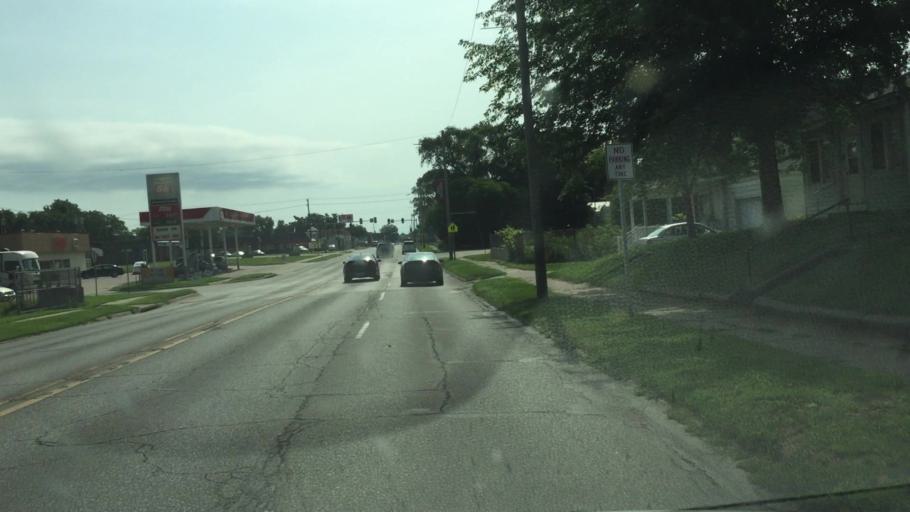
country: US
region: Iowa
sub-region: Lee County
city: Fort Madison
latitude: 40.6301
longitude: -91.3271
